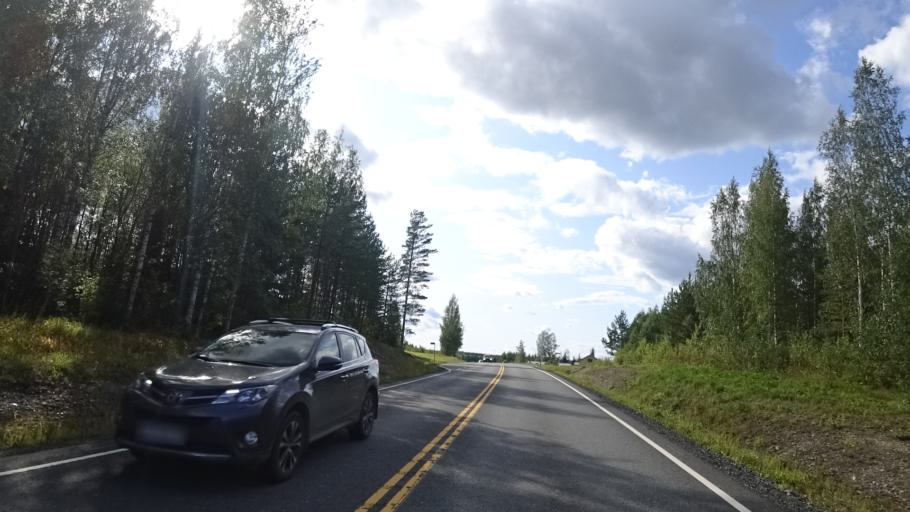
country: FI
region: North Karelia
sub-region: Keski-Karjala
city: Tohmajaervi
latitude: 62.1853
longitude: 30.4967
